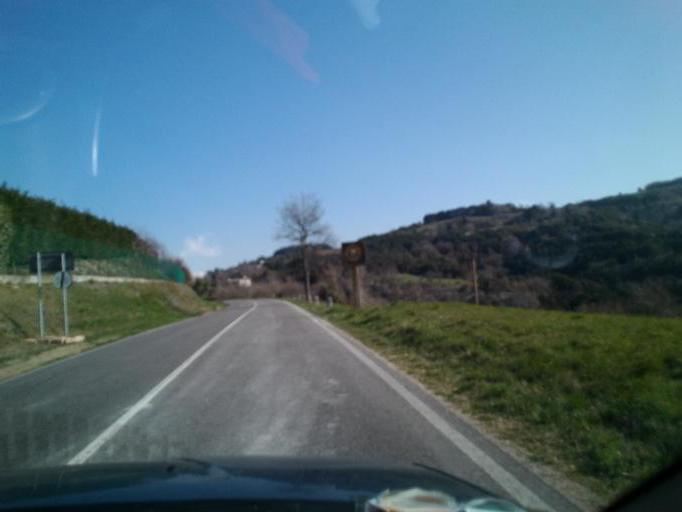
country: IT
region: Veneto
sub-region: Provincia di Verona
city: Cerro Veronese
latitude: 45.5534
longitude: 11.0348
